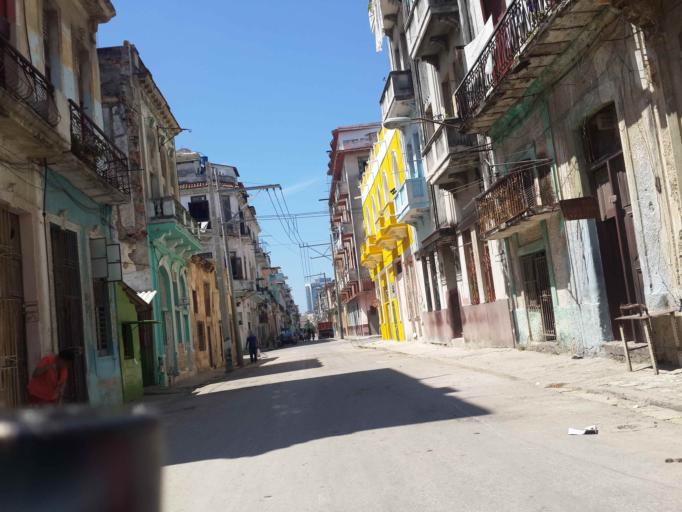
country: CU
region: La Habana
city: Centro Habana
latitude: 23.1405
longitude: -82.3667
